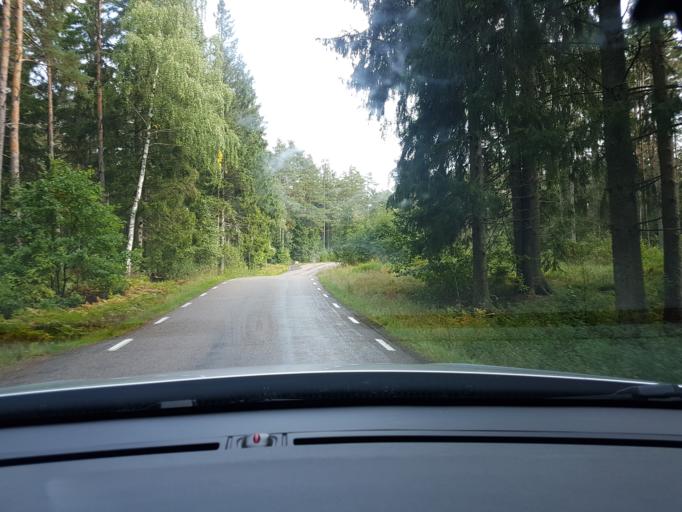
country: SE
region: Vaestra Goetaland
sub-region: Ale Kommun
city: Alvangen
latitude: 57.9078
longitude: 12.1661
